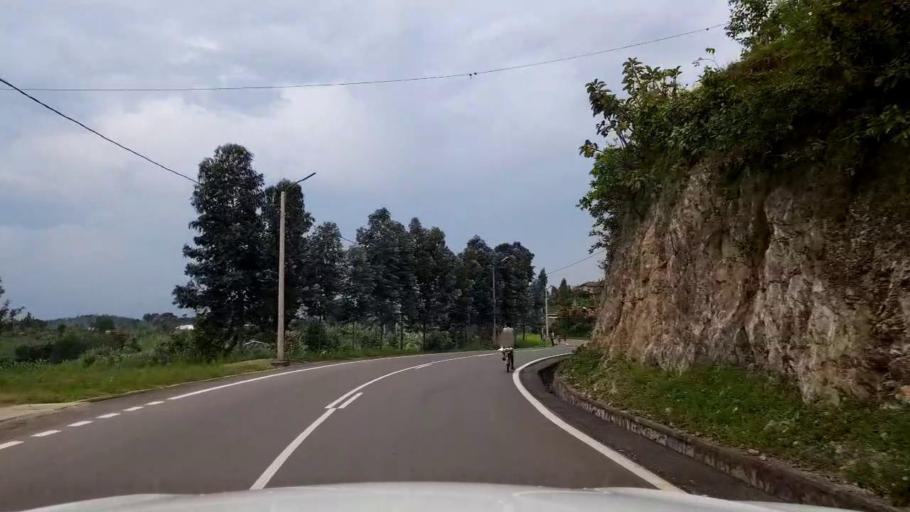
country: RW
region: Western Province
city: Kibuye
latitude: -2.0447
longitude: 29.4085
